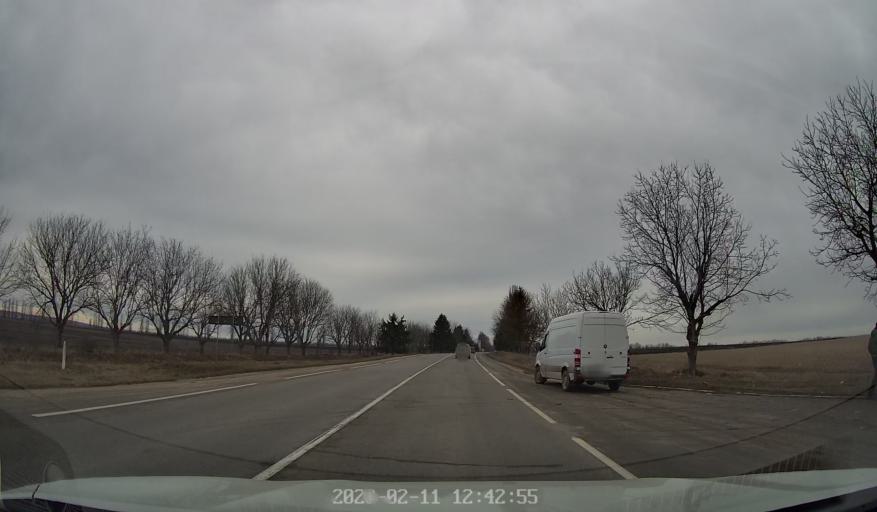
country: MD
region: Raionul Edinet
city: Edinet
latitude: 48.2274
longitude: 27.2157
